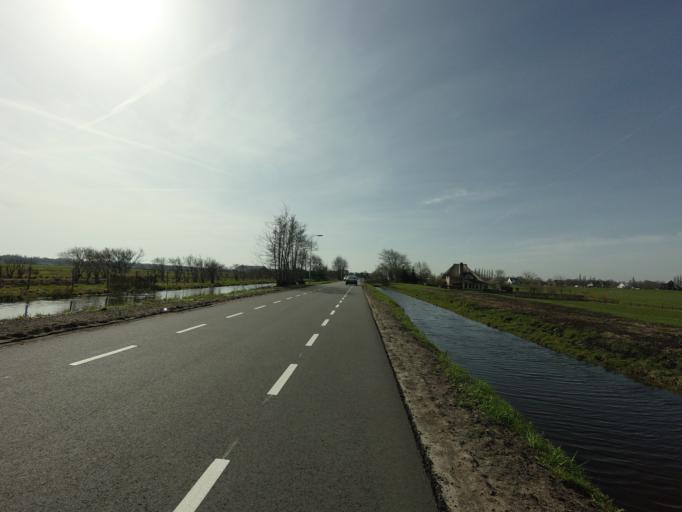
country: NL
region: South Holland
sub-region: Gemeente Gouda
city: Bloemendaal
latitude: 52.0468
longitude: 4.6883
